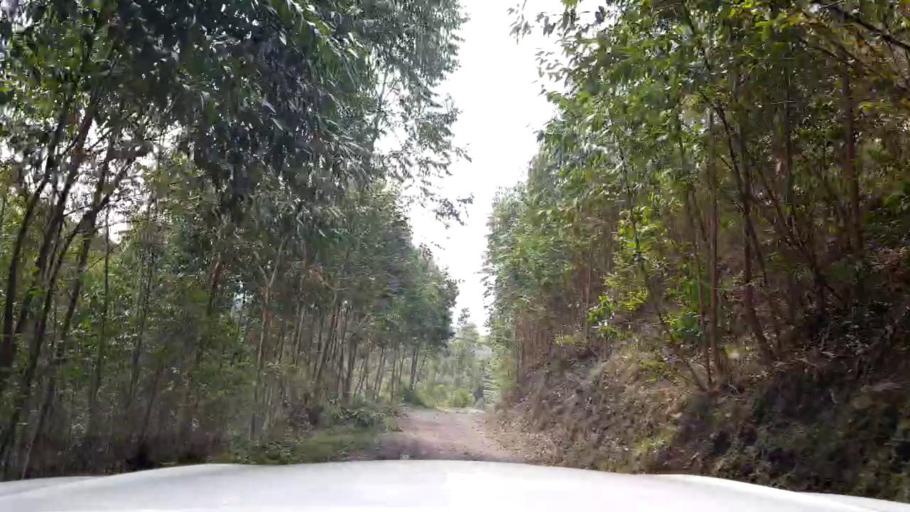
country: RW
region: Northern Province
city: Byumba
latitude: -1.5209
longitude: 30.1290
